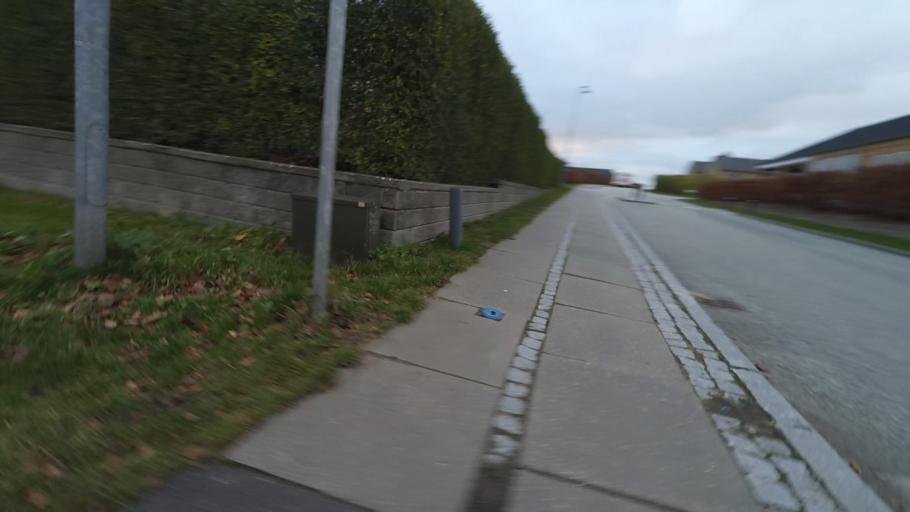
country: DK
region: Central Jutland
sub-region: Arhus Kommune
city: Stavtrup
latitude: 56.1603
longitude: 10.0939
